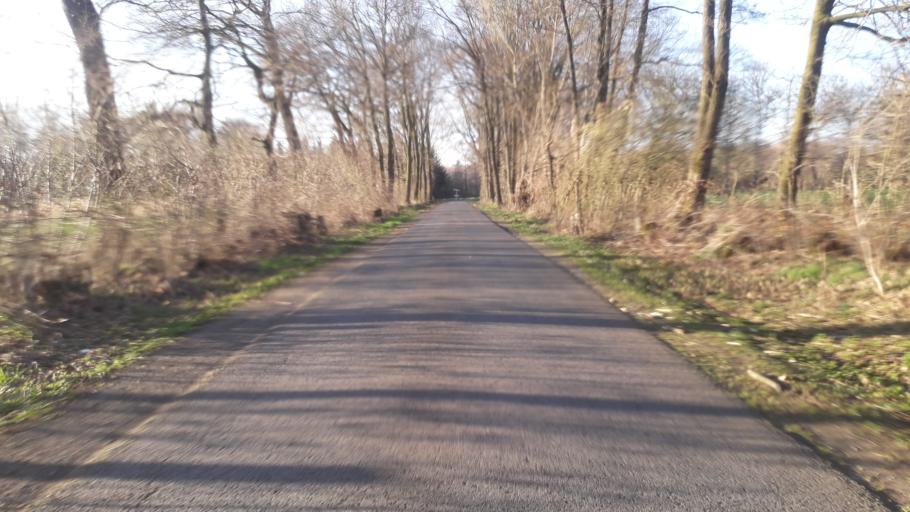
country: DE
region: North Rhine-Westphalia
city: Rietberg
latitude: 51.7868
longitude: 8.4651
